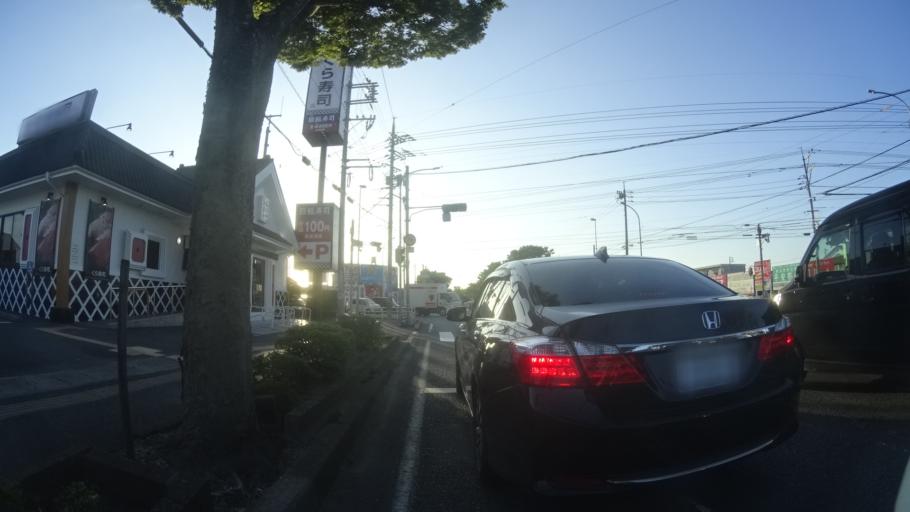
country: JP
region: Tottori
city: Yonago
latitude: 35.4513
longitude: 133.3580
